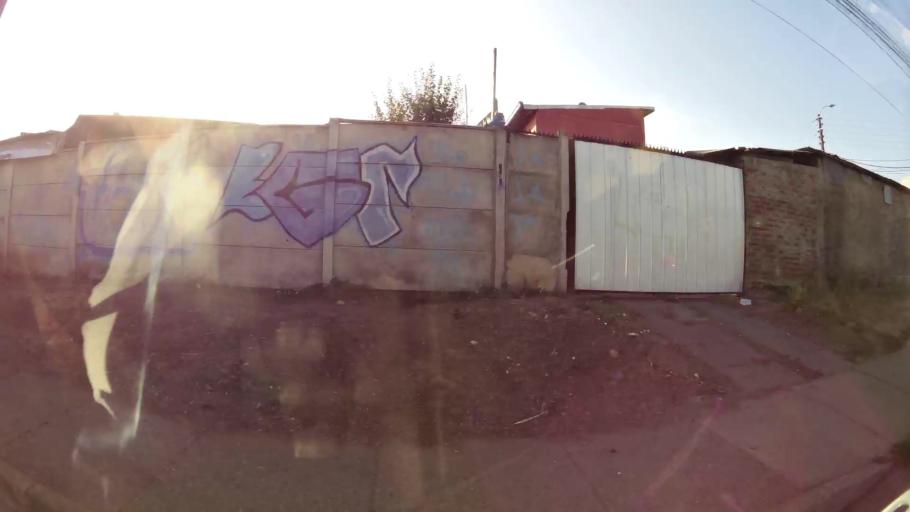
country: CL
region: Maule
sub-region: Provincia de Talca
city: Talca
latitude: -35.4065
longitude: -71.6534
